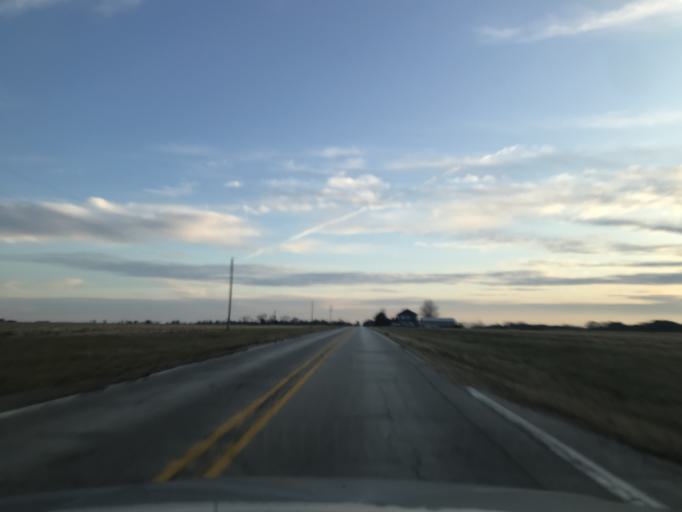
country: US
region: Illinois
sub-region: Henderson County
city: Oquawka
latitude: 40.9708
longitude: -90.8639
